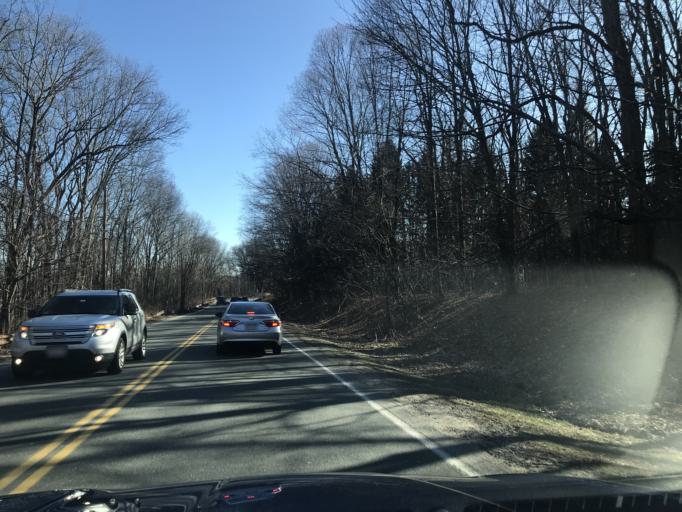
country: US
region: Massachusetts
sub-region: Essex County
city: North Andover
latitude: 42.7079
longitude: -71.0736
